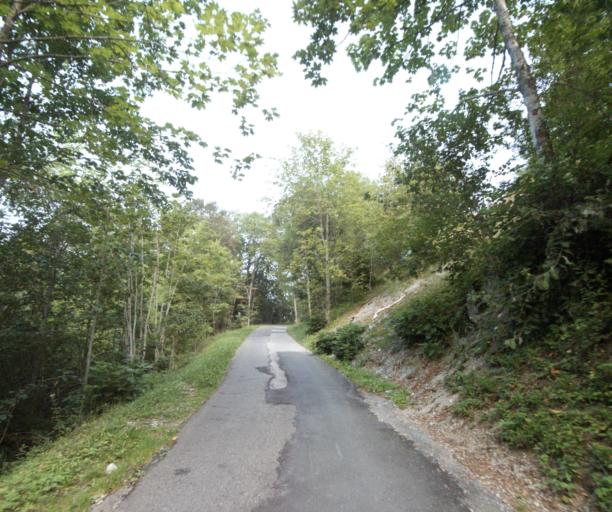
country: CH
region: Vaud
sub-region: Riviera-Pays-d'Enhaut District
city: Caux
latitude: 46.4131
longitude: 6.9444
